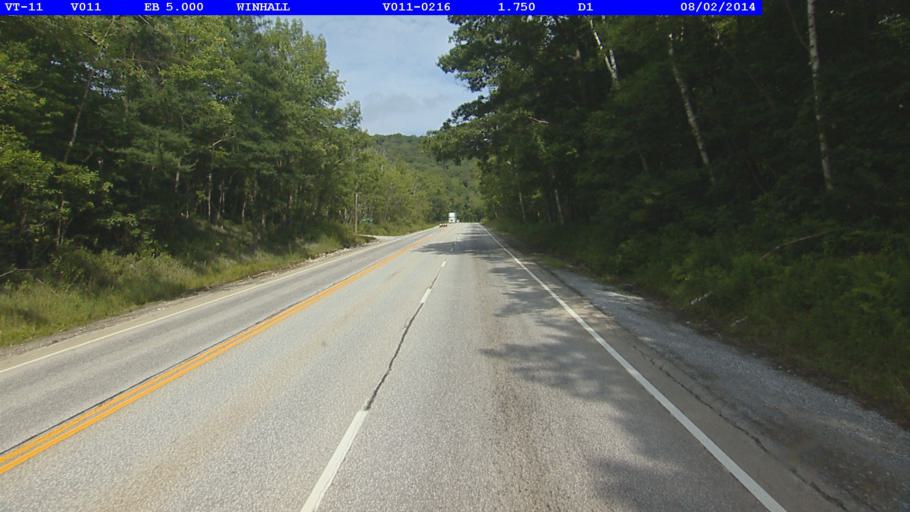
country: US
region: Vermont
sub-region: Bennington County
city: Manchester Center
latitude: 43.2067
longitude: -72.9864
